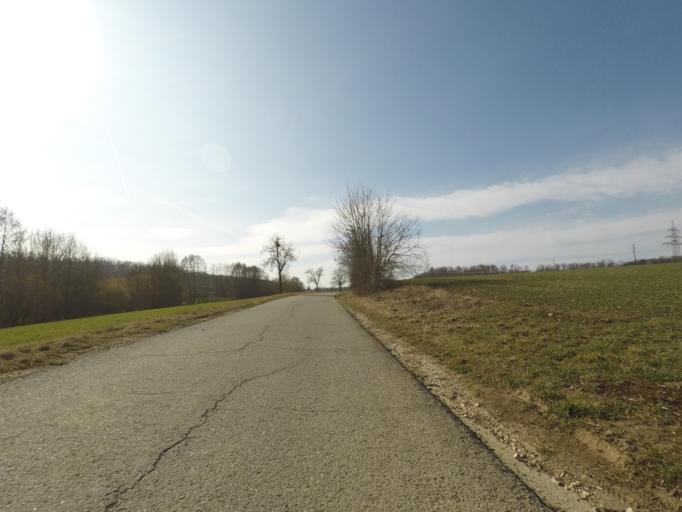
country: DE
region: Baden-Wuerttemberg
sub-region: Tuebingen Region
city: Metzingen
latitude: 48.5298
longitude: 9.2615
